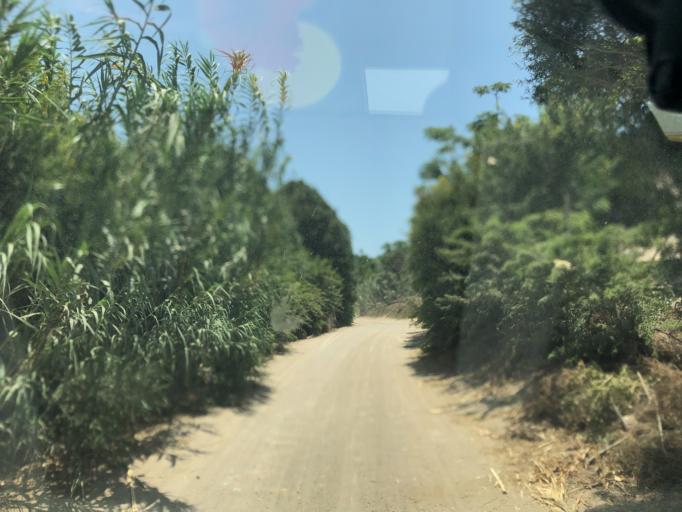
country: PE
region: Lima
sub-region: Provincia de Canete
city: Quilmana
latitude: -13.0067
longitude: -76.4574
